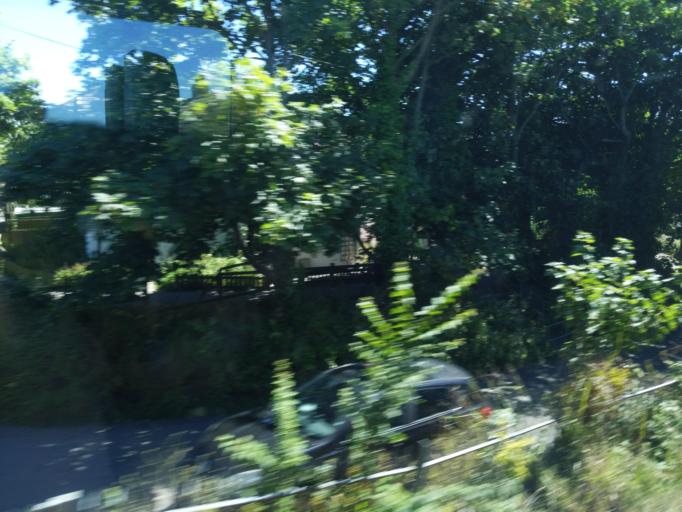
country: GB
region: England
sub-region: Cornwall
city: Hayle
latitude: 50.1901
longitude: -5.4062
